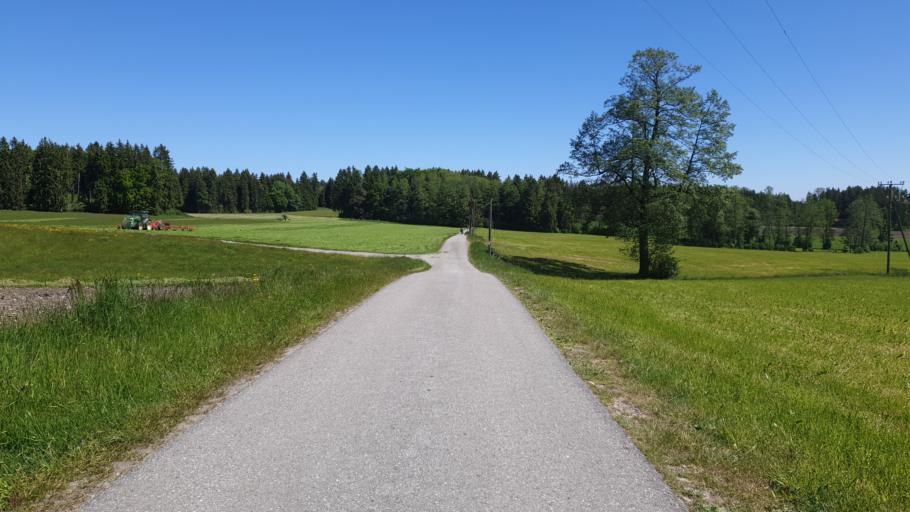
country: DE
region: Bavaria
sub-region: Upper Bavaria
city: Habach
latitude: 47.7510
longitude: 11.2586
